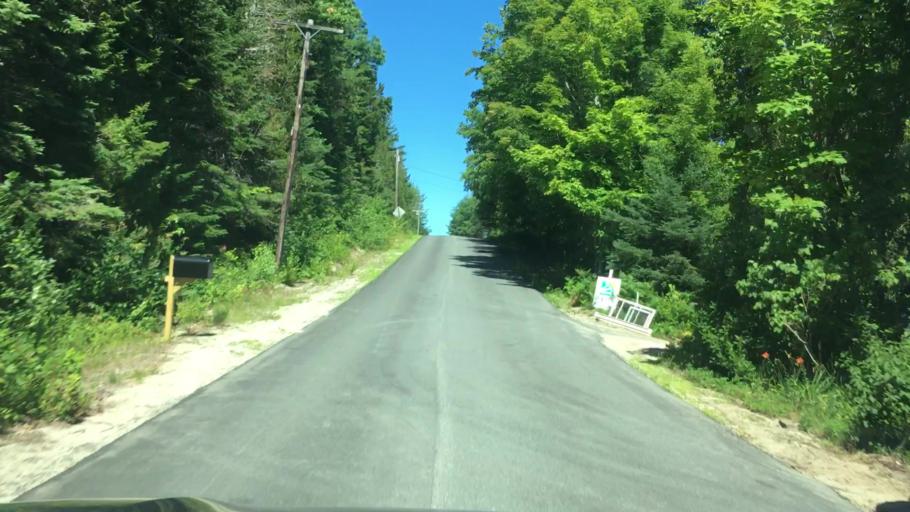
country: US
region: Maine
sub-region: Hancock County
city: Sedgwick
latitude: 44.3183
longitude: -68.6249
